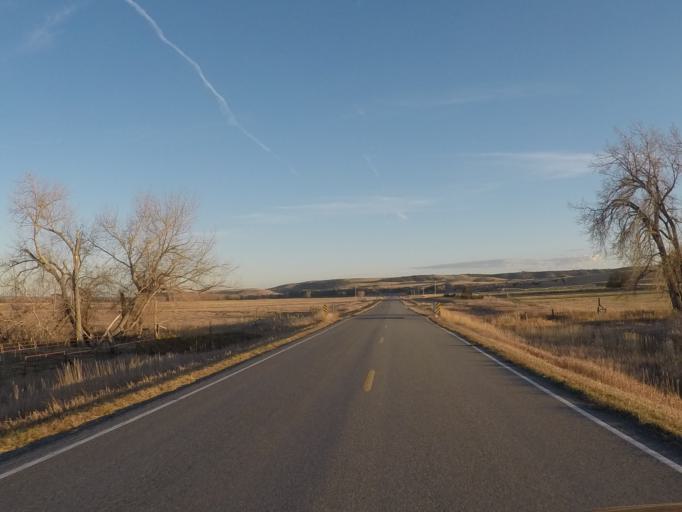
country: US
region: Montana
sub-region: Sweet Grass County
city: Big Timber
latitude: 45.7987
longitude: -109.8608
